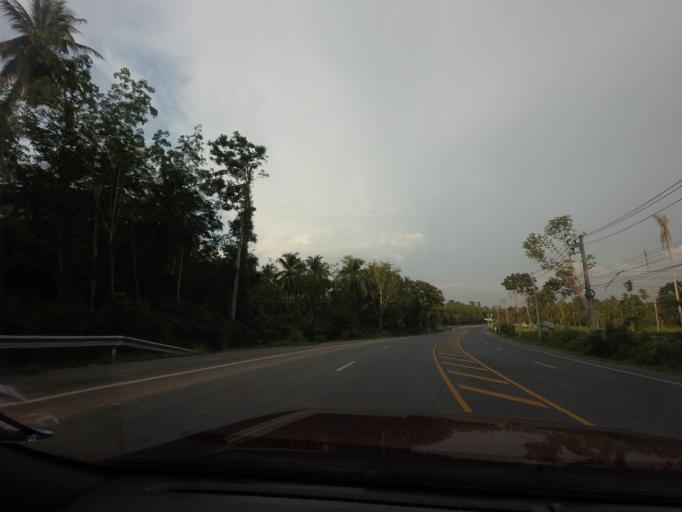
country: TH
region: Pattani
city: Khok Pho
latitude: 6.6774
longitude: 101.1218
